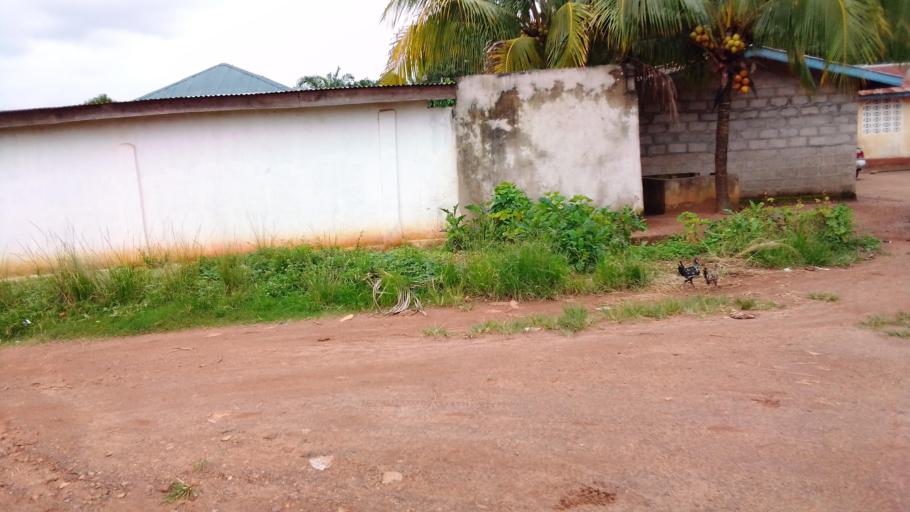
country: SL
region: Eastern Province
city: Kenema
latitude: 7.8527
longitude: -11.1930
